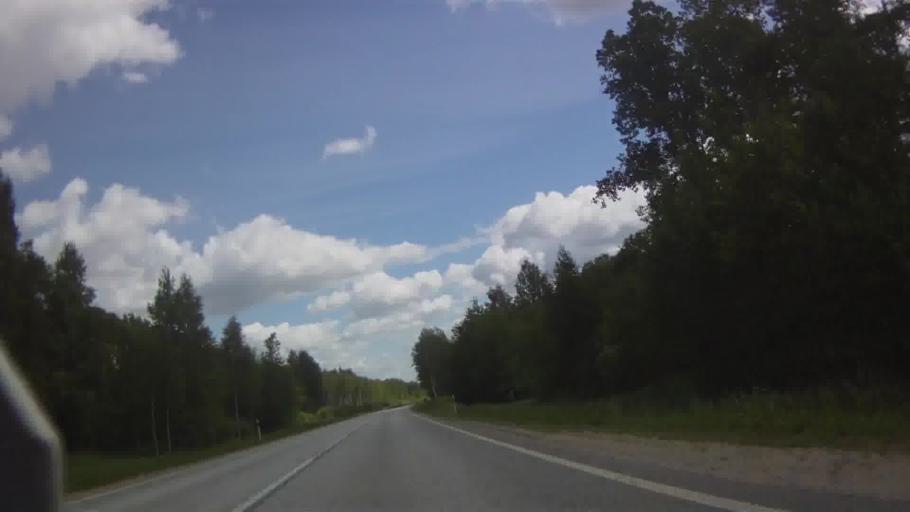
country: LV
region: Varaklani
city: Varaklani
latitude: 56.5242
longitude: 26.4812
